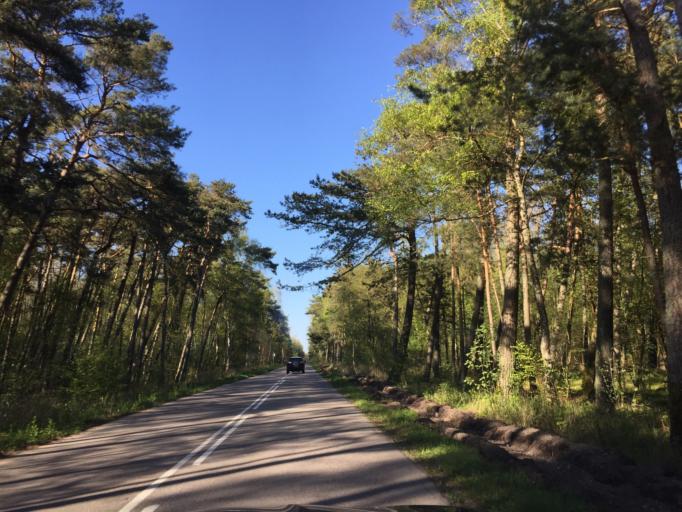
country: LT
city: Nida
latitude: 55.2039
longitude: 20.8730
